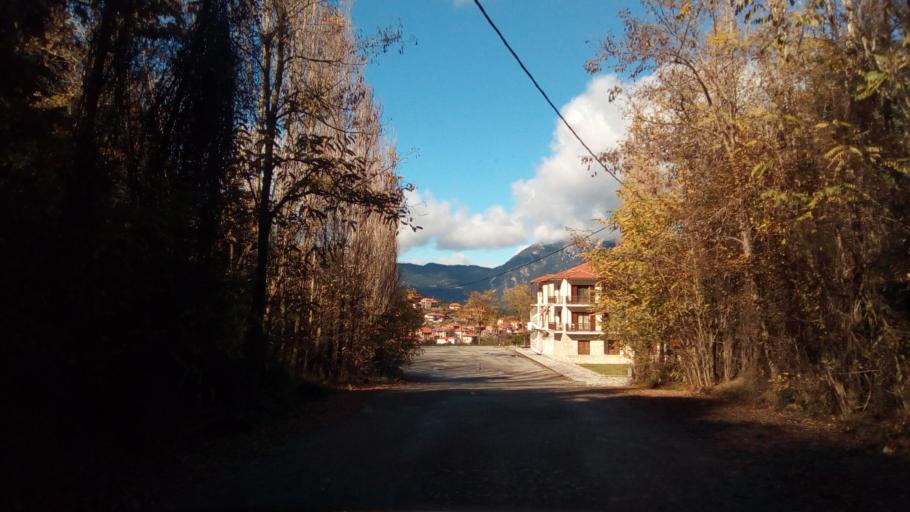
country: GR
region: West Greece
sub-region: Nomos Aitolias kai Akarnanias
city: Nafpaktos
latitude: 38.5876
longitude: 21.9293
